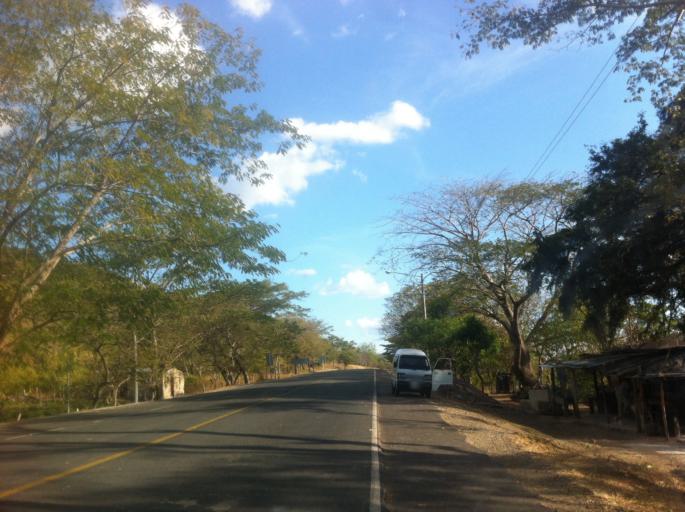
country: NI
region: Chontales
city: Acoyapa
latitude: 12.0024
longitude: -85.1626
